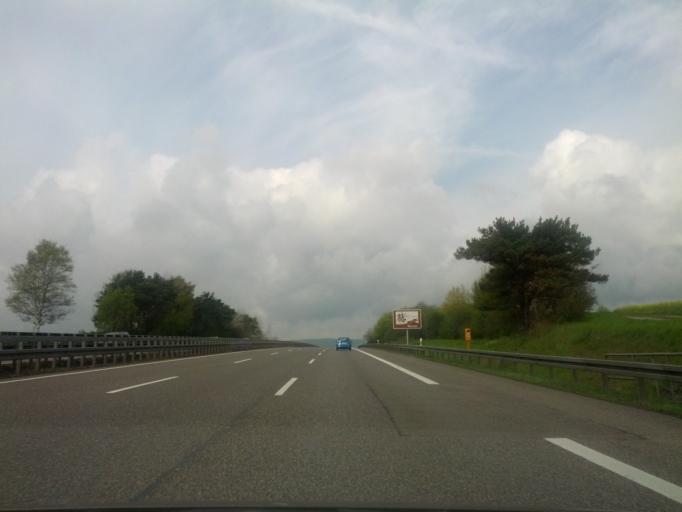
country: DE
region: Hesse
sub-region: Regierungsbezirk Kassel
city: Herleshausen
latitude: 51.0129
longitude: 10.1513
